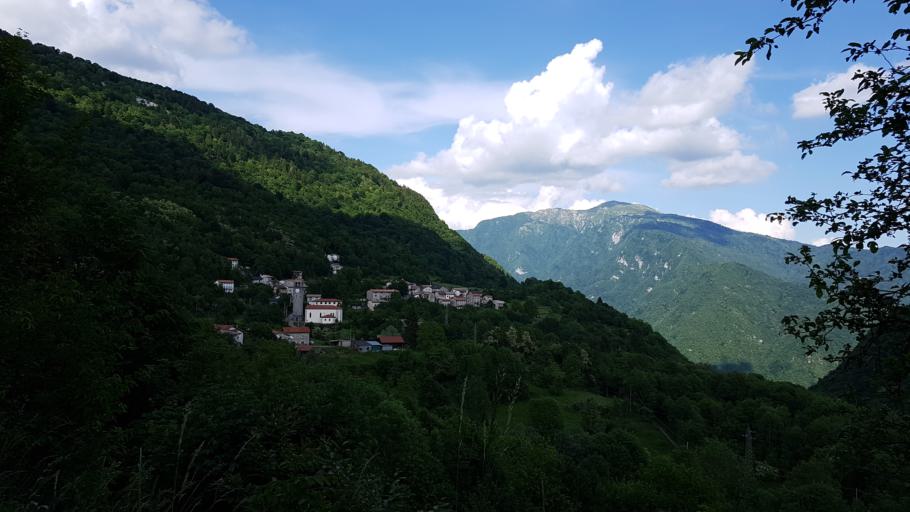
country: IT
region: Friuli Venezia Giulia
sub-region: Provincia di Udine
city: Pulfero
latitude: 46.1955
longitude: 13.4372
